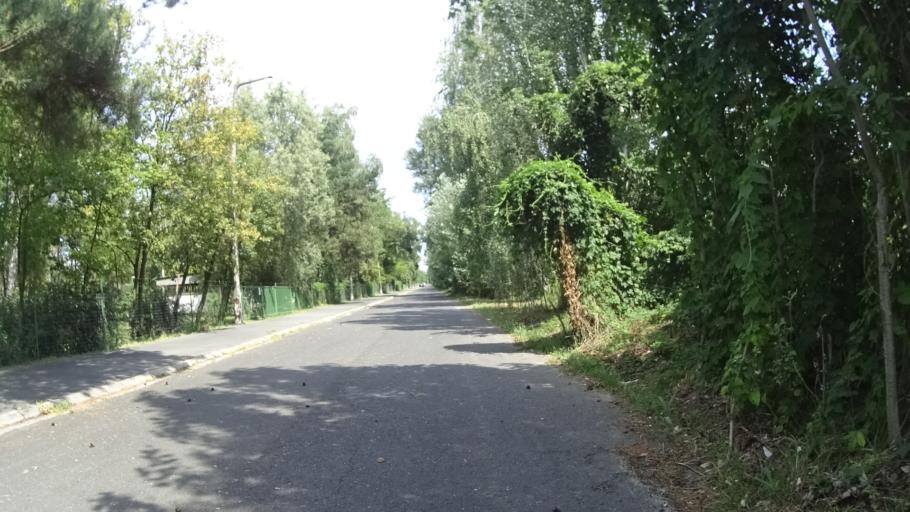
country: HU
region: Somogy
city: Fonyod
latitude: 46.7636
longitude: 17.6063
